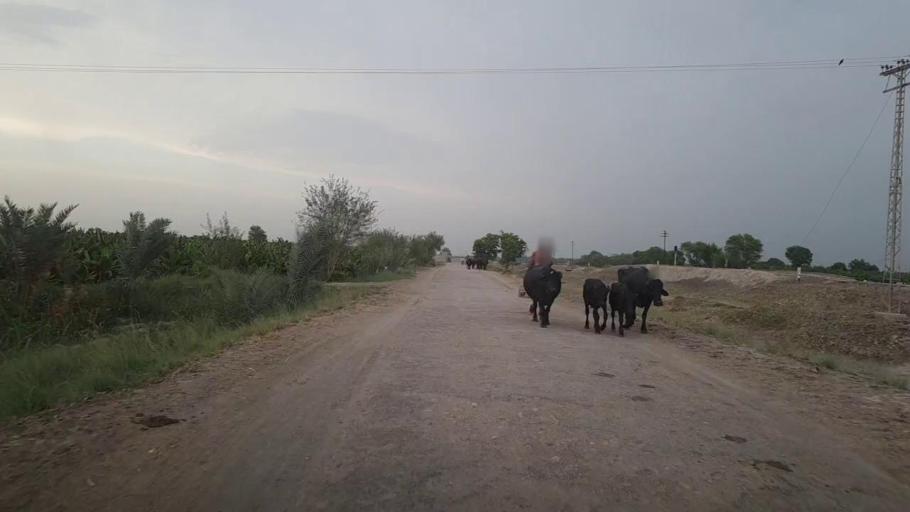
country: PK
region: Sindh
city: Karaundi
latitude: 26.9934
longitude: 68.3468
